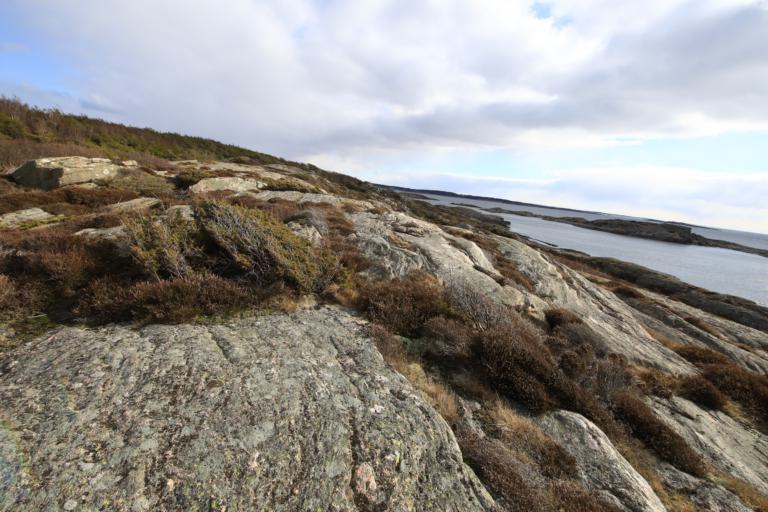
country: SE
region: Halland
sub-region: Kungsbacka Kommun
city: Frillesas
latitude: 57.2165
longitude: 12.1363
